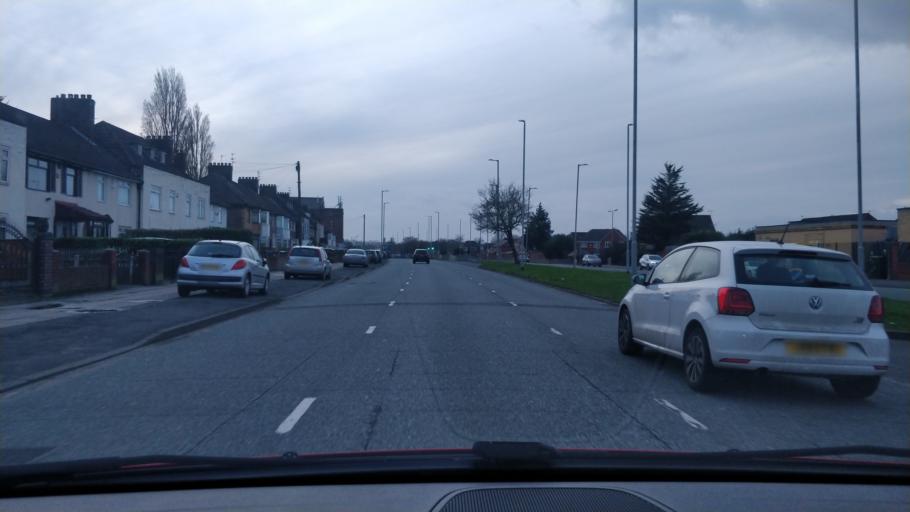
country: GB
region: England
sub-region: Knowsley
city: Huyton
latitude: 53.4203
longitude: -2.8710
